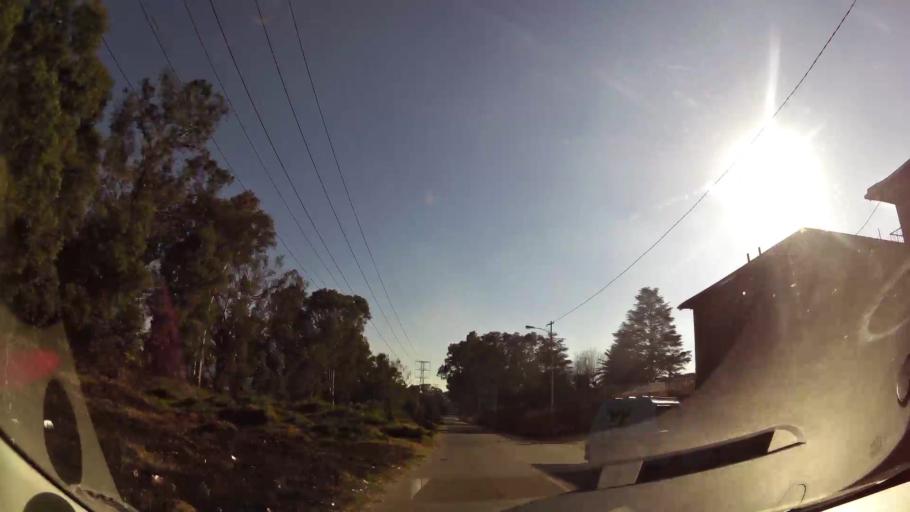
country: ZA
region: Gauteng
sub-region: City of Johannesburg Metropolitan Municipality
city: Roodepoort
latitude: -26.1605
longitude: 27.8578
